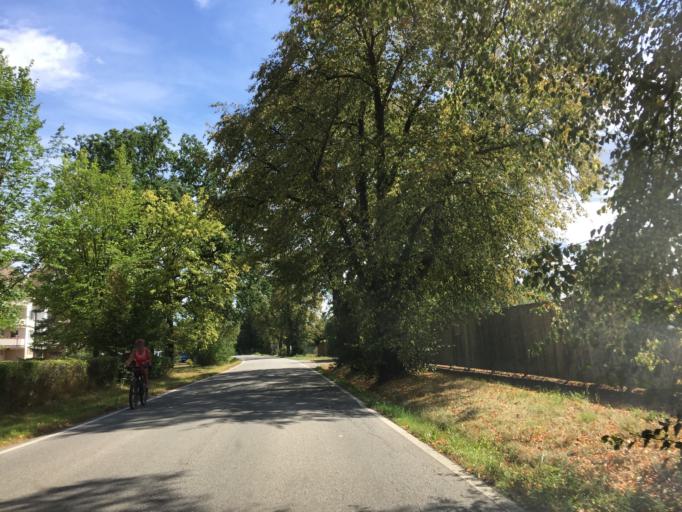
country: CZ
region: Jihocesky
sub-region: Okres Ceske Budejovice
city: Ceske Budejovice
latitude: 48.9564
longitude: 14.4772
